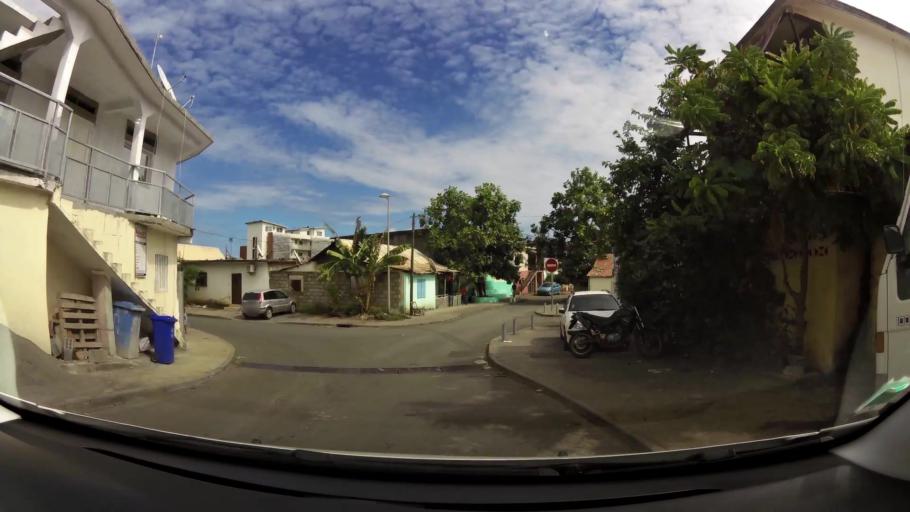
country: YT
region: Mamoudzou
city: Mamoudzou
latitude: -12.7818
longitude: 45.2336
